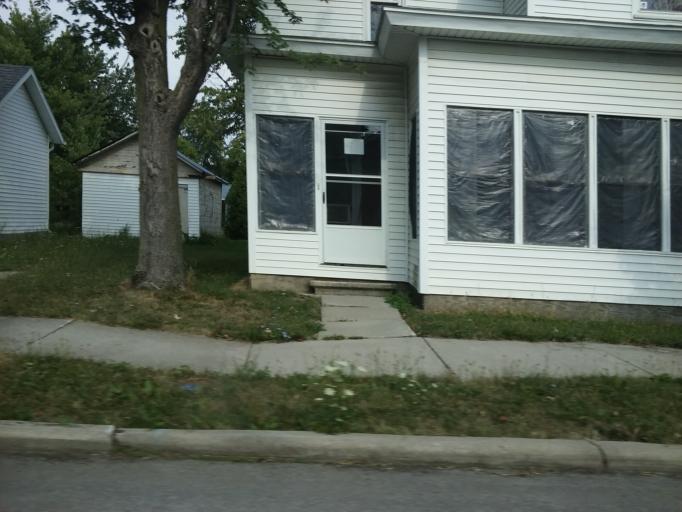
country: US
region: Ohio
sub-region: Hancock County
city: McComb
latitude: 41.1911
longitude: -83.7844
